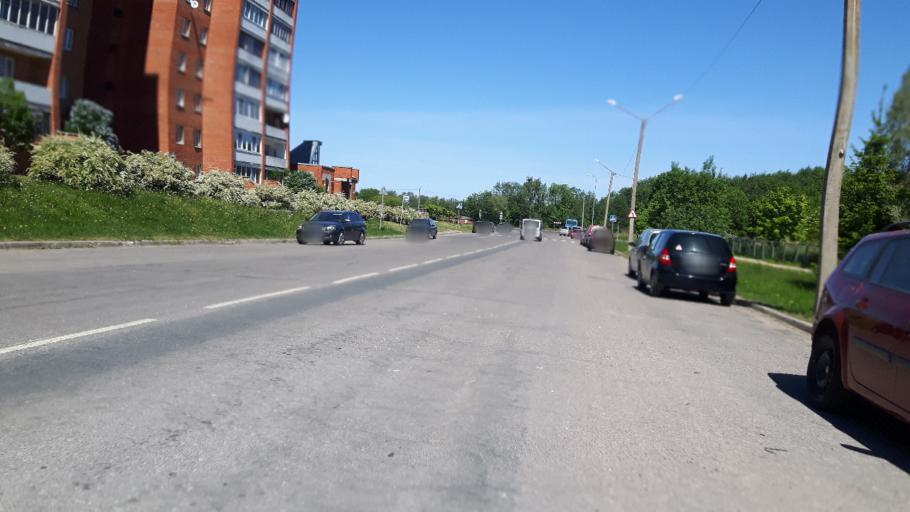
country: EE
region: Ida-Virumaa
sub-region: Sillamaee linn
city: Sillamae
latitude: 59.3926
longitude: 27.7971
